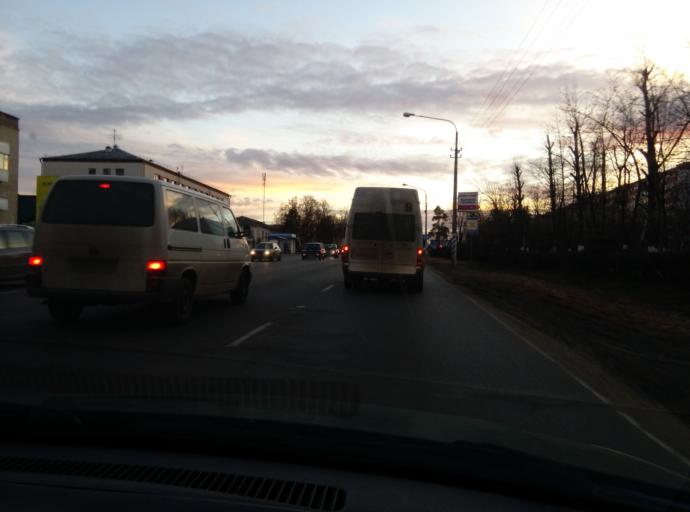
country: BY
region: Minsk
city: Horad Barysaw
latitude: 54.2152
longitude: 28.4890
